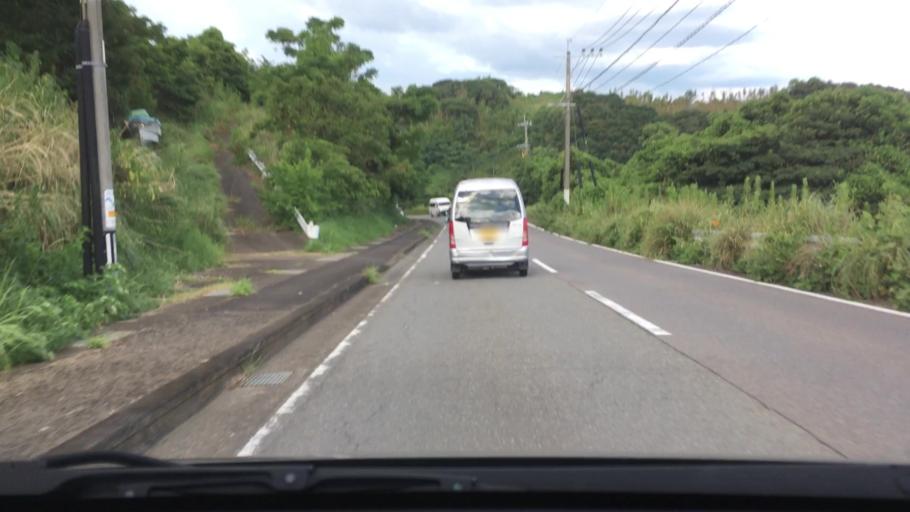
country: JP
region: Nagasaki
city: Togitsu
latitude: 32.8193
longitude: 129.7392
